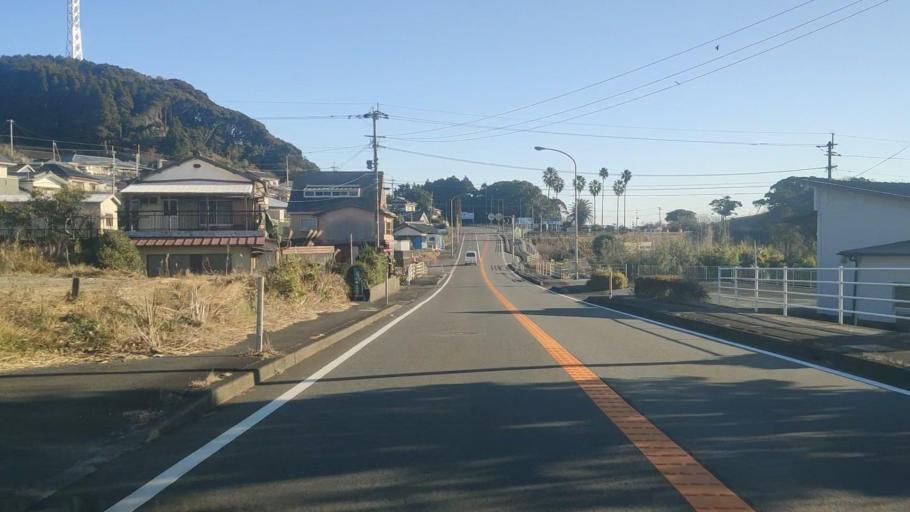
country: JP
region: Miyazaki
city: Takanabe
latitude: 32.3423
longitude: 131.6209
